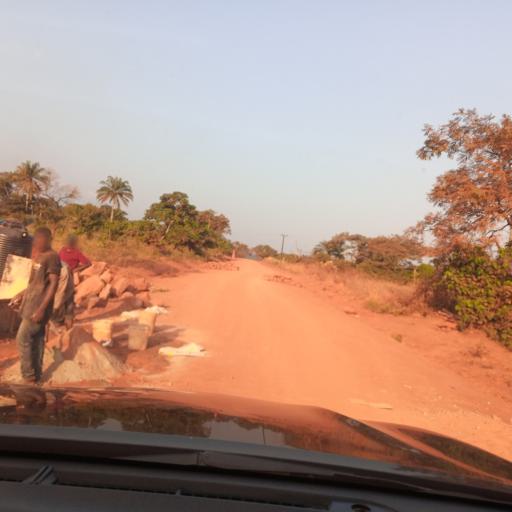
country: NG
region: Enugu
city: Aku
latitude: 6.7161
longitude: 7.3463
